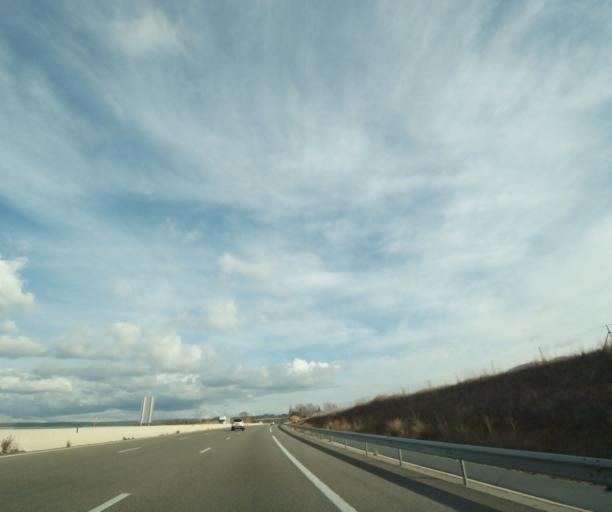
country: FR
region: Provence-Alpes-Cote d'Azur
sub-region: Departement du Var
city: Pourrieres
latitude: 43.4770
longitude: 5.7094
